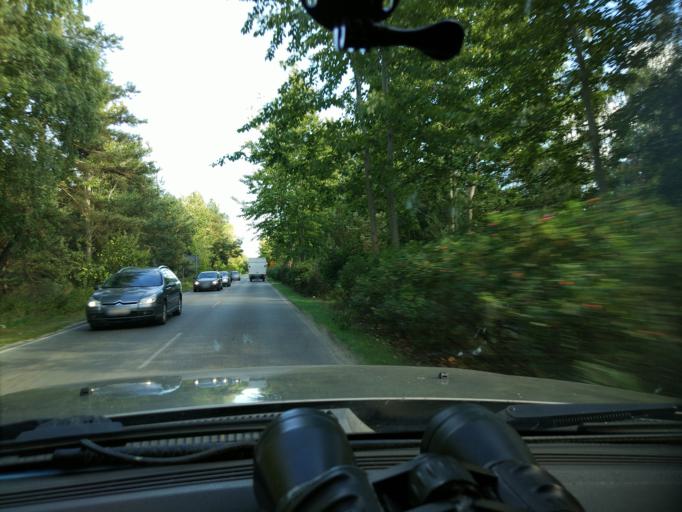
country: PL
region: Pomeranian Voivodeship
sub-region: Powiat pucki
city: Wladyslawowo
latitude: 54.7883
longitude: 18.4284
